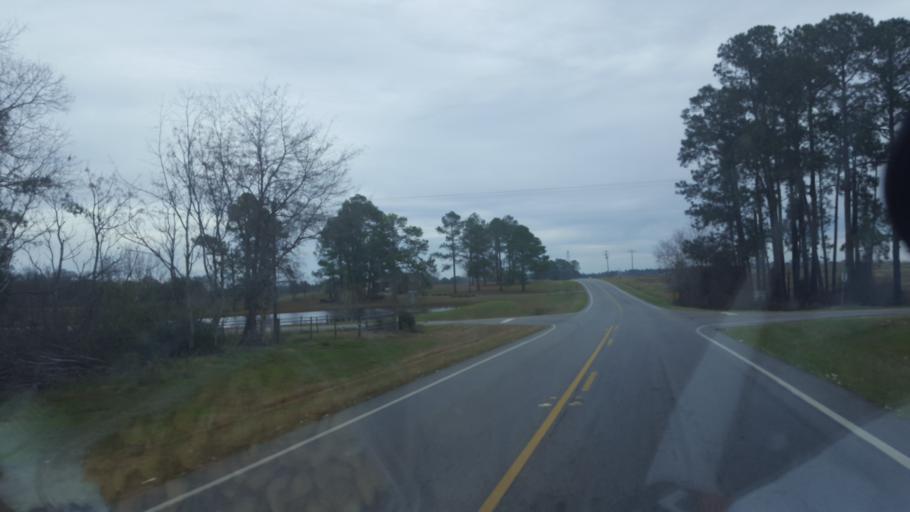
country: US
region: Georgia
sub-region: Turner County
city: Ashburn
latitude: 31.7161
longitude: -83.6113
